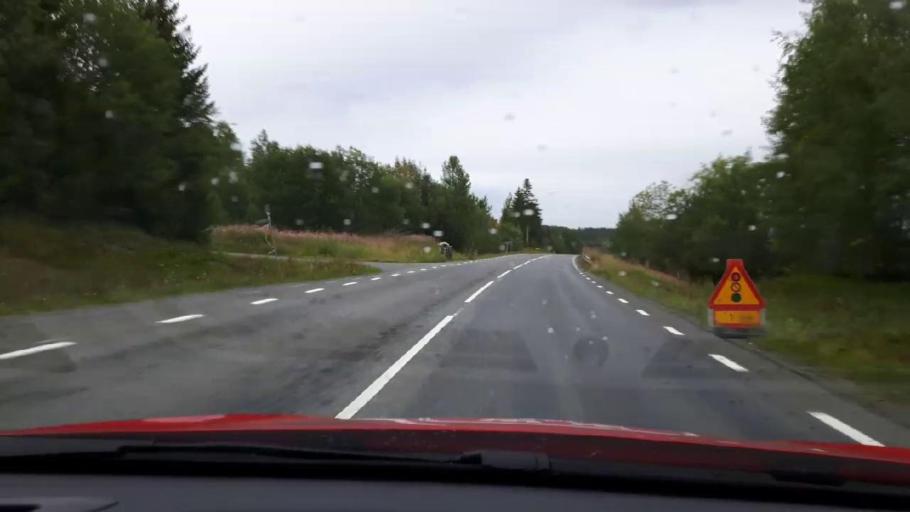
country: SE
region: Jaemtland
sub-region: Are Kommun
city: Jarpen
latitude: 63.3843
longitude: 13.4176
